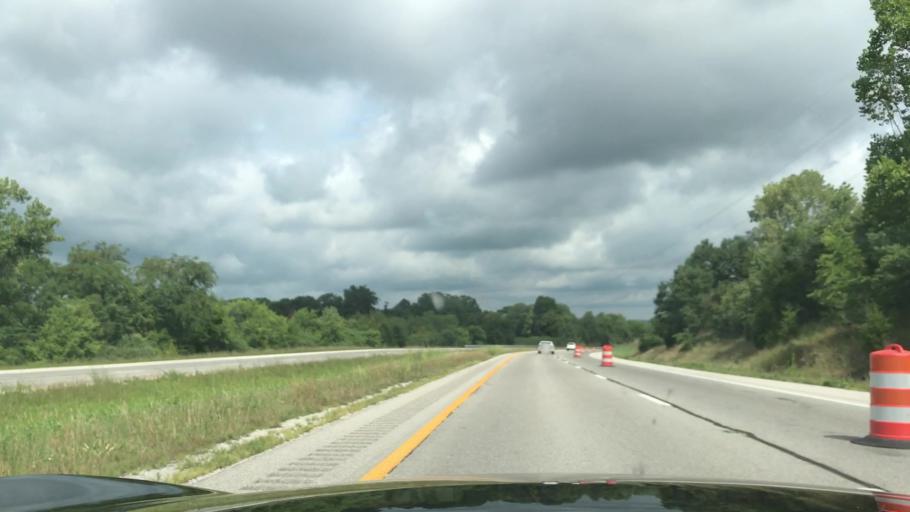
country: US
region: Kentucky
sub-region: Butler County
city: Morgantown
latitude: 37.0991
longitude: -86.6363
